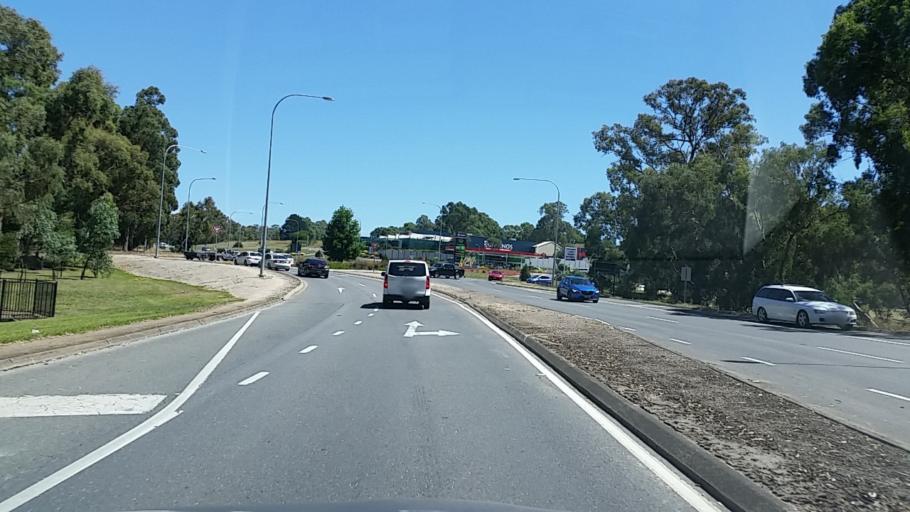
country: AU
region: South Australia
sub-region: Mount Barker
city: Little Hampton
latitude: -35.0543
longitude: 138.8539
